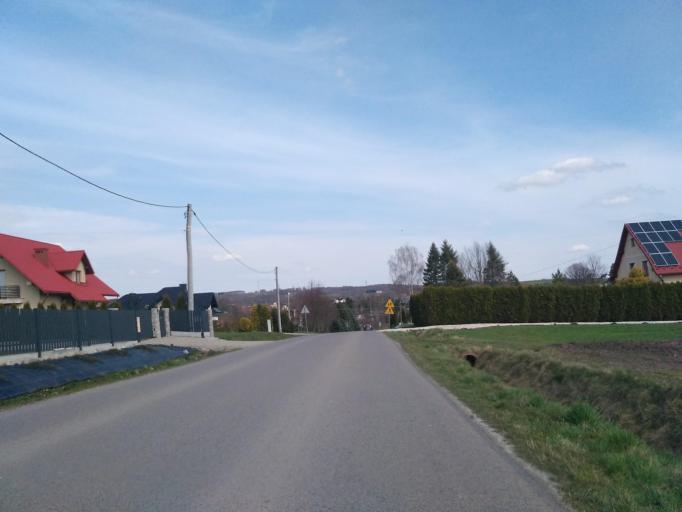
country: PL
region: Subcarpathian Voivodeship
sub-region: Powiat ropczycko-sedziszowski
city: Iwierzyce
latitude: 50.0168
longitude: 21.7850
